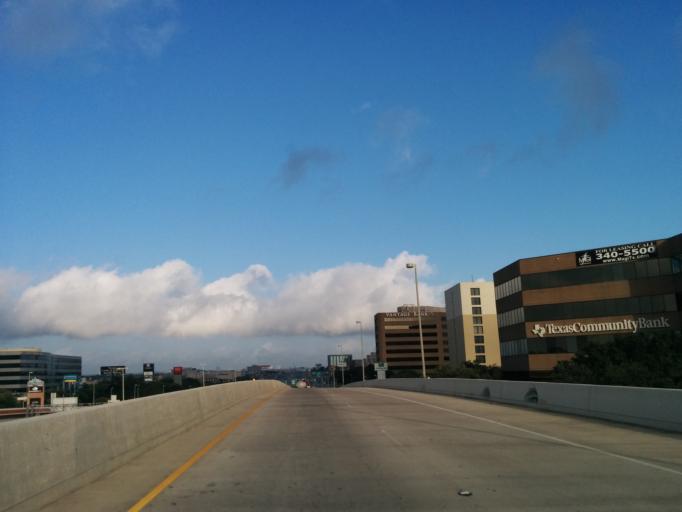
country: US
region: Texas
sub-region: Bexar County
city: Castle Hills
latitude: 29.5206
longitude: -98.4867
